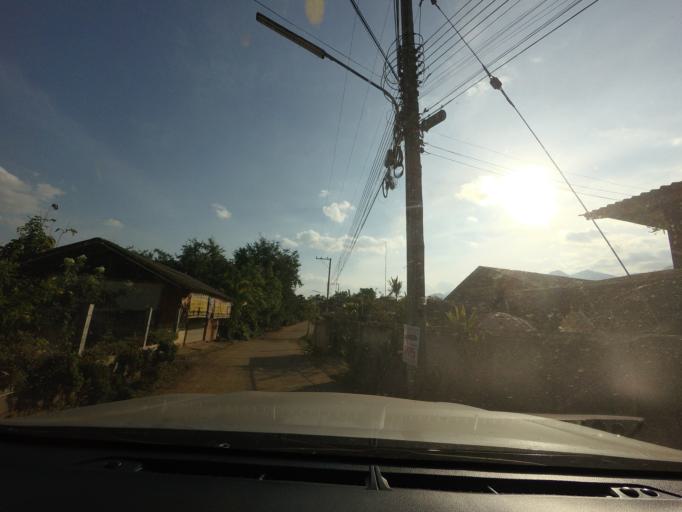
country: TH
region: Mae Hong Son
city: Wiang Nuea
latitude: 19.3985
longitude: 98.4047
